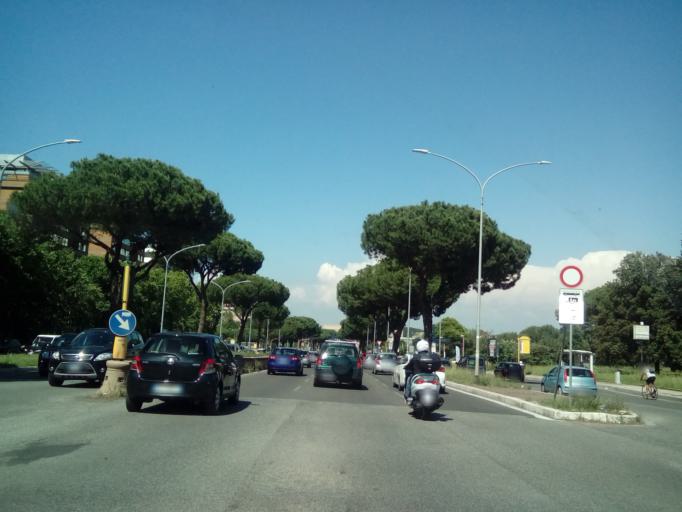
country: IT
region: Latium
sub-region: Citta metropolitana di Roma Capitale
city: Rome
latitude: 41.8509
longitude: 12.4859
